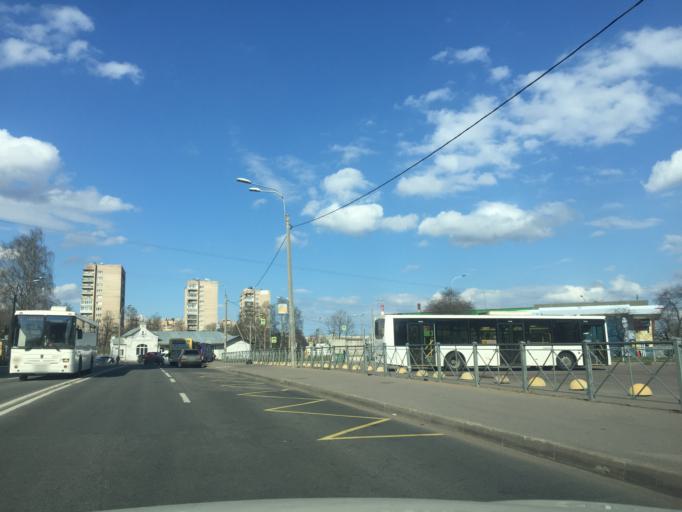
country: RU
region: Leningrad
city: Kalininskiy
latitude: 59.9866
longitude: 30.4249
